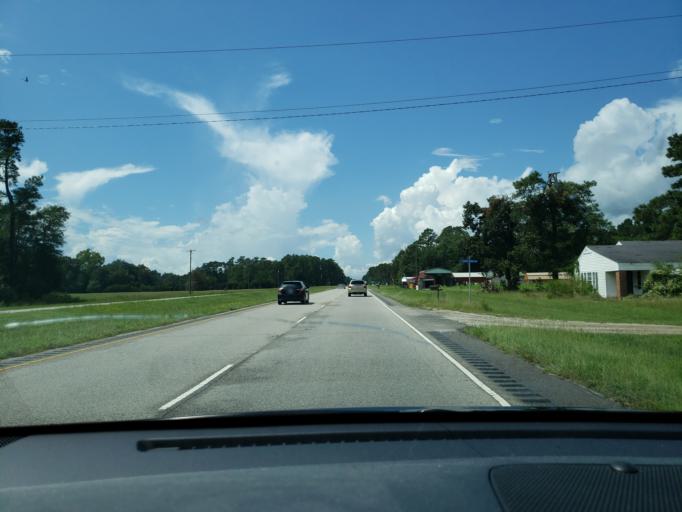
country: US
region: North Carolina
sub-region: Bladen County
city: Elizabethtown
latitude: 34.6454
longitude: -78.6982
